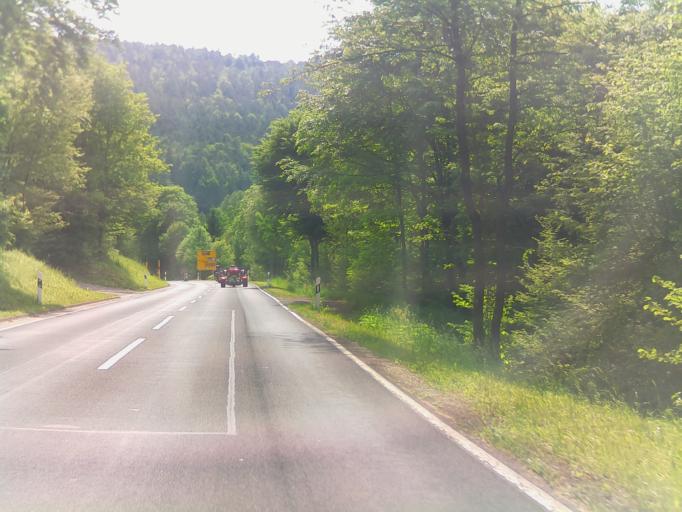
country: DE
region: Bavaria
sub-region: Regierungsbezirk Unterfranken
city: Hasloch
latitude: 49.8188
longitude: 9.4976
